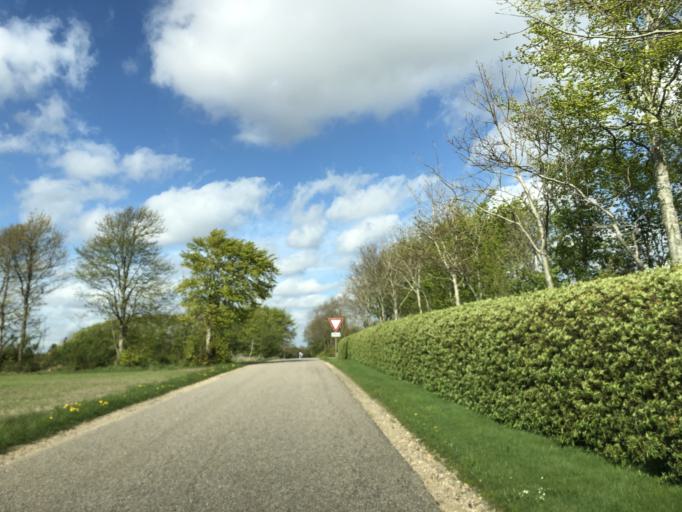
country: DK
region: Central Jutland
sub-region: Herning Kommune
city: Avlum
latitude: 56.3050
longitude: 8.7007
